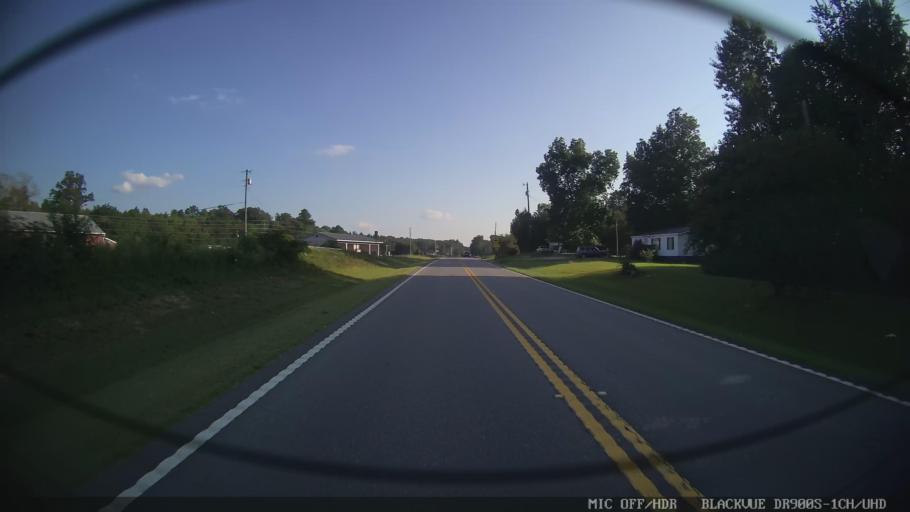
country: US
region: Tennessee
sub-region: Bradley County
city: Wildwood Lake
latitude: 34.9627
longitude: -84.7732
